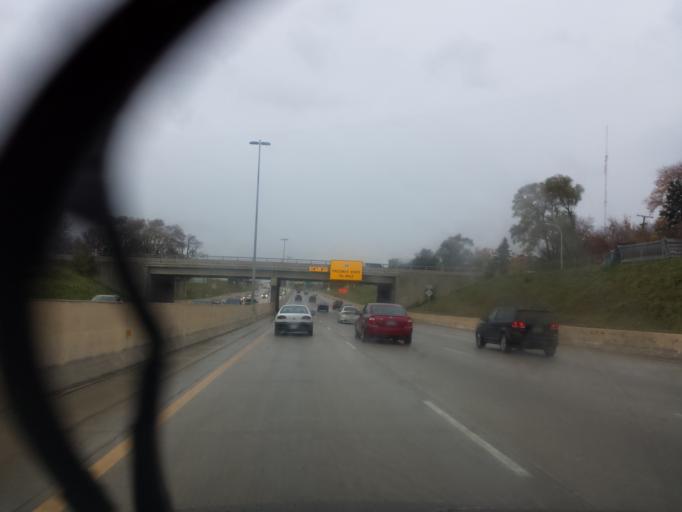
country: US
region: Michigan
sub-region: Oakland County
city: Southfield
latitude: 42.4505
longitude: -83.2199
